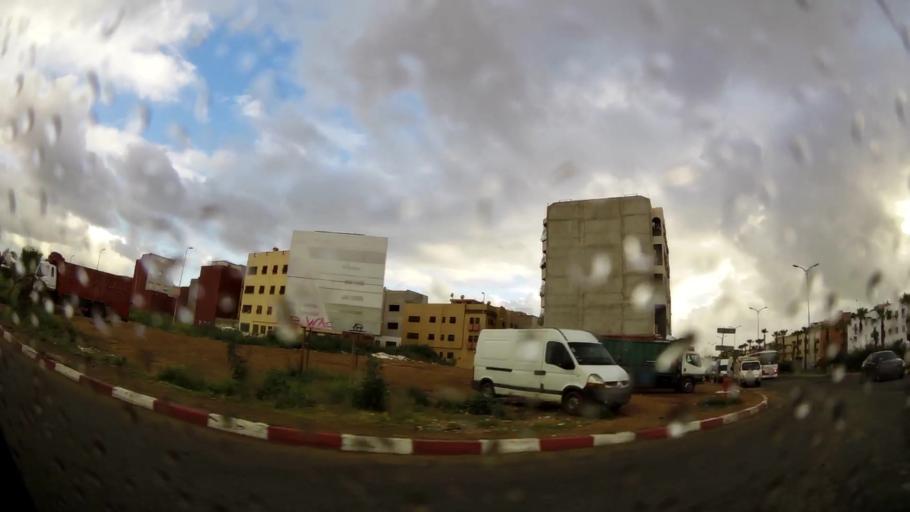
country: MA
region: Grand Casablanca
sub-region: Mohammedia
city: Mohammedia
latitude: 33.6834
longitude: -7.3857
